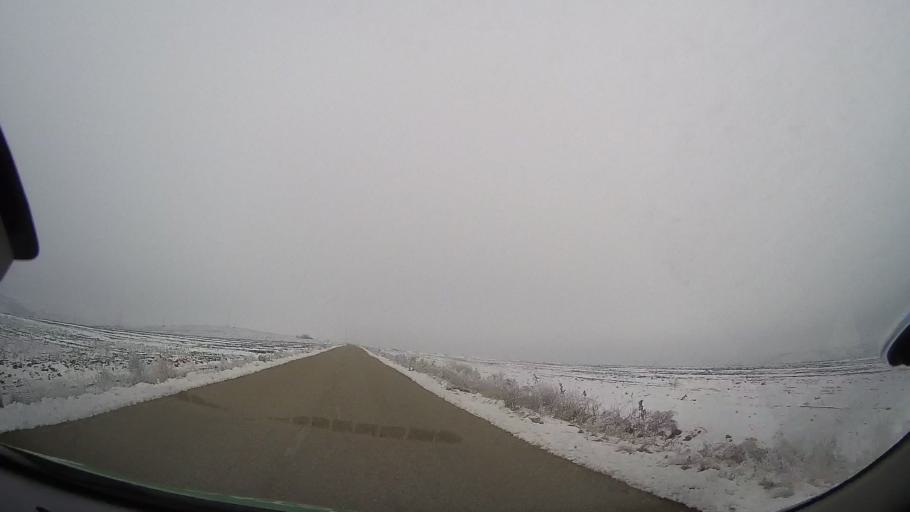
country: RO
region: Vaslui
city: Coroiesti
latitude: 46.2262
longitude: 27.4784
